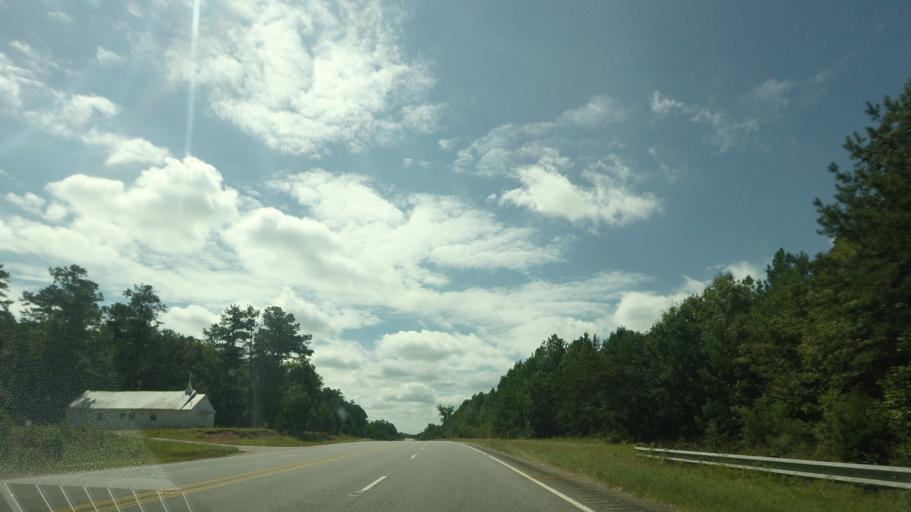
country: US
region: Georgia
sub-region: Houston County
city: Robins Air Force Base
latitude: 32.5370
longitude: -83.4407
